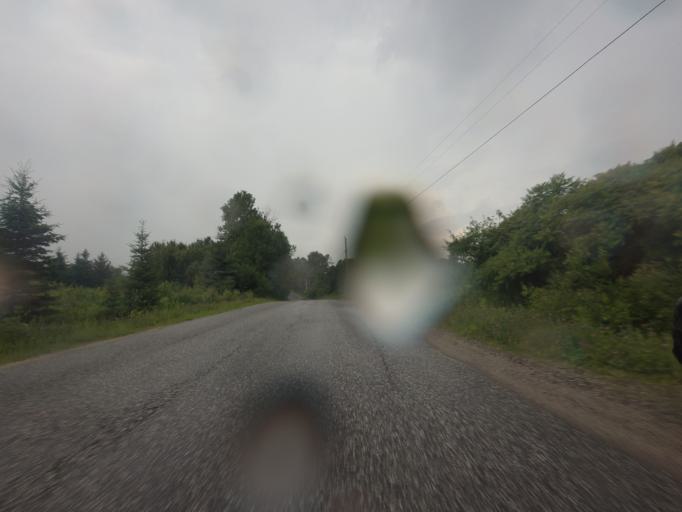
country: CA
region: Quebec
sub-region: Outaouais
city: Maniwaki
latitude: 46.4267
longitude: -75.9525
